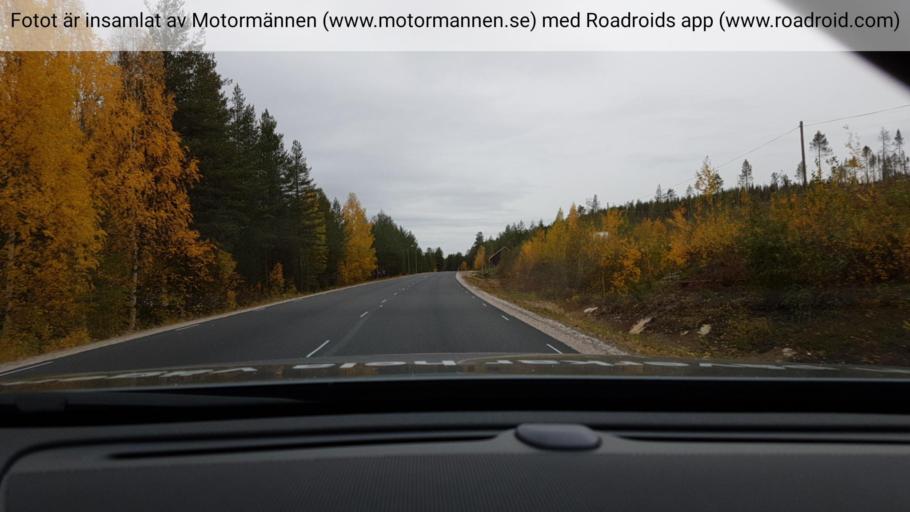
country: SE
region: Norrbotten
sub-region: Overkalix Kommun
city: OEverkalix
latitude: 66.3901
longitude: 22.8211
